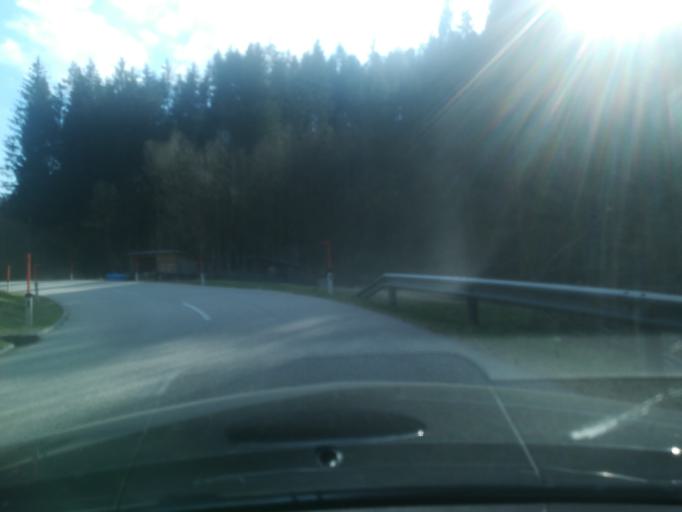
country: AT
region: Upper Austria
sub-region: Politischer Bezirk Freistadt
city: Freistadt
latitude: 48.4208
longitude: 14.6373
